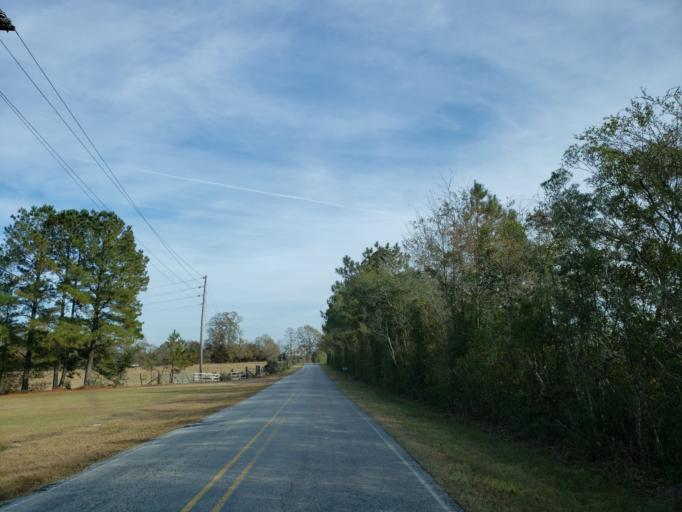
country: US
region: Mississippi
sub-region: Forrest County
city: Rawls Springs
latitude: 31.4085
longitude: -89.4065
